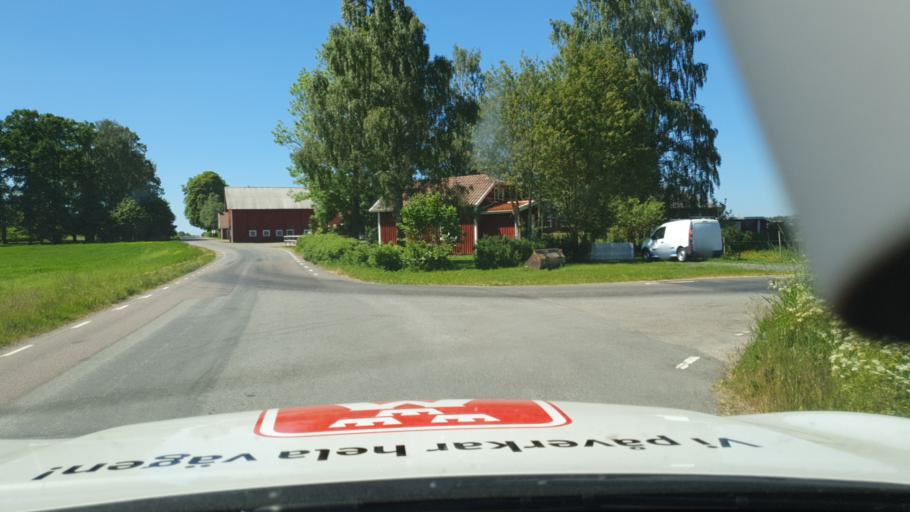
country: SE
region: Joenkoeping
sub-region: Habo Kommun
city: Habo
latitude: 57.8990
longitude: 14.0482
